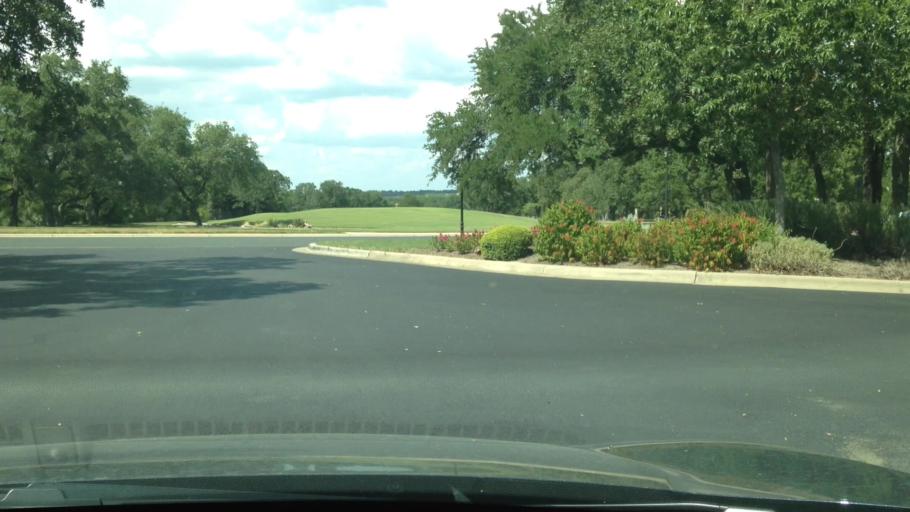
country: US
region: Texas
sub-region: Williamson County
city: Leander
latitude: 30.6395
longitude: -97.7942
